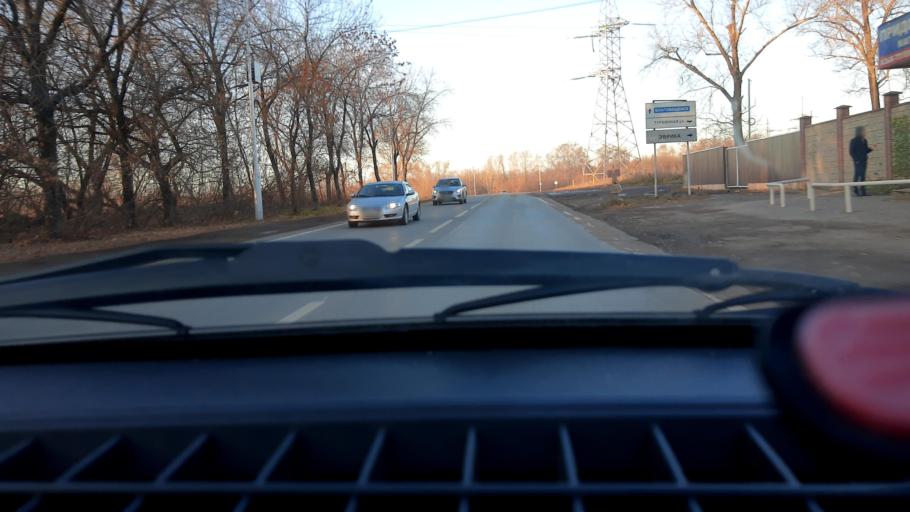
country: RU
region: Bashkortostan
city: Blagoveshchensk
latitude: 54.9017
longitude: 56.0537
